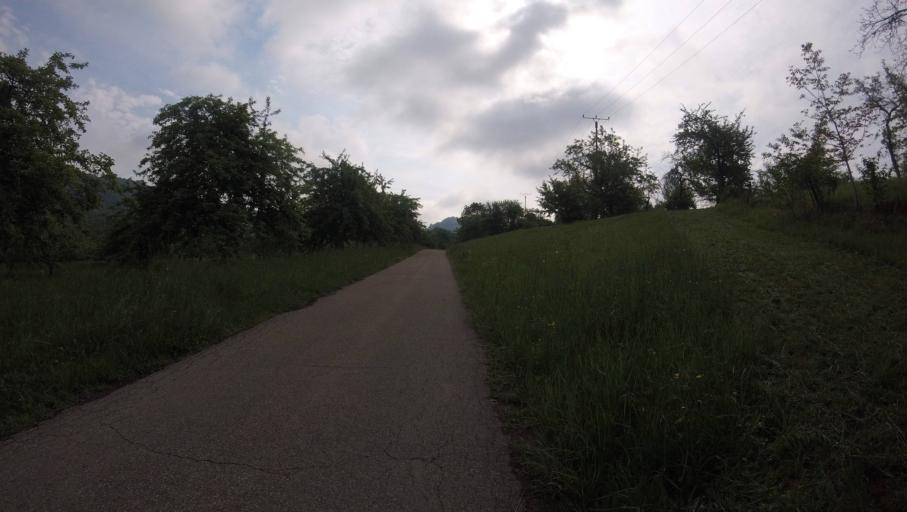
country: DE
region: Baden-Wuerttemberg
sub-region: Regierungsbezirk Stuttgart
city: Allmersbach im Tal
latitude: 48.9374
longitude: 9.5111
